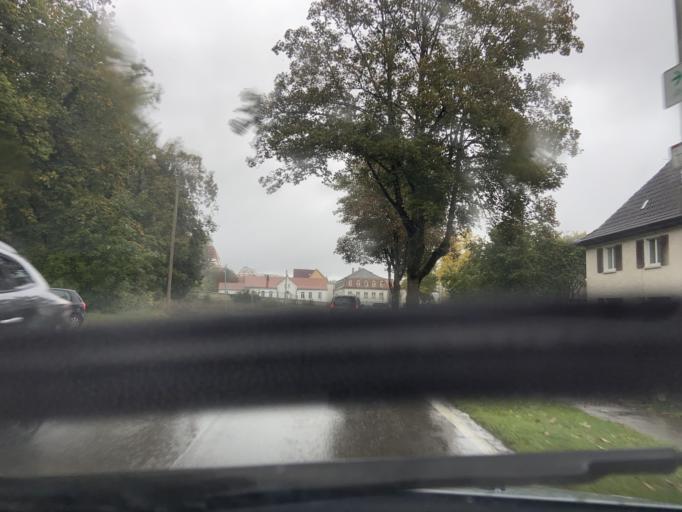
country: DE
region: Baden-Wuerttemberg
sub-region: Tuebingen Region
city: Scheer
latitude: 48.0707
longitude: 9.2951
